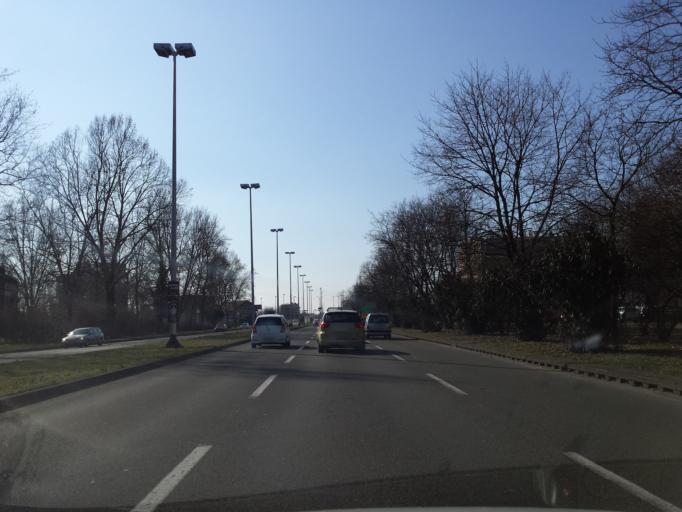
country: HR
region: Grad Zagreb
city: Novi Zagreb
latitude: 45.7632
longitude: 15.9906
